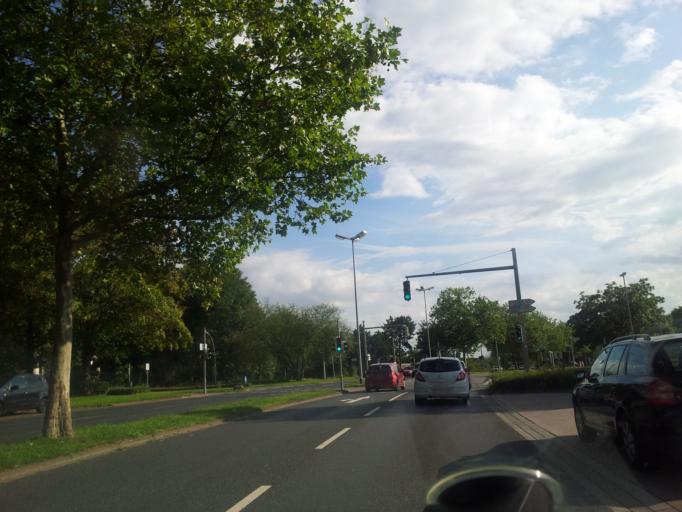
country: DE
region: Lower Saxony
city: Braunschweig
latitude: 52.2313
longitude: 10.5372
